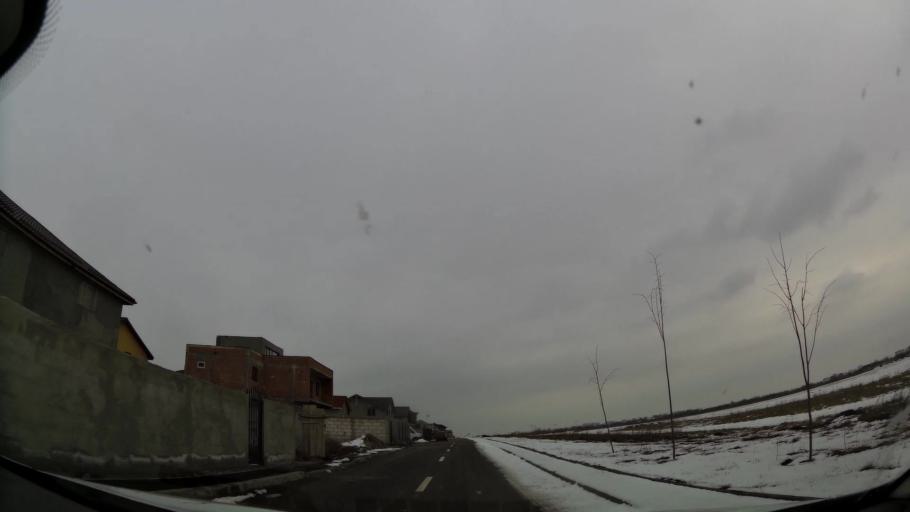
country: RO
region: Ilfov
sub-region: Comuna Tunari
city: Tunari
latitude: 44.5520
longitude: 26.1519
